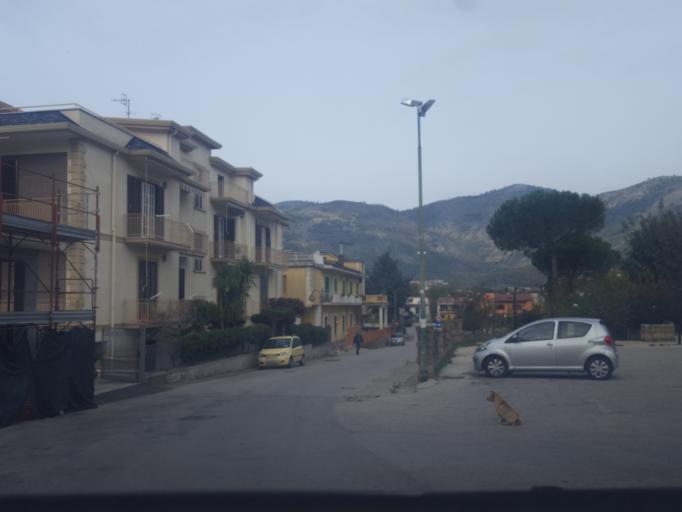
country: IT
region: Campania
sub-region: Provincia di Caserta
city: Arienzo
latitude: 41.0232
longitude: 14.4975
